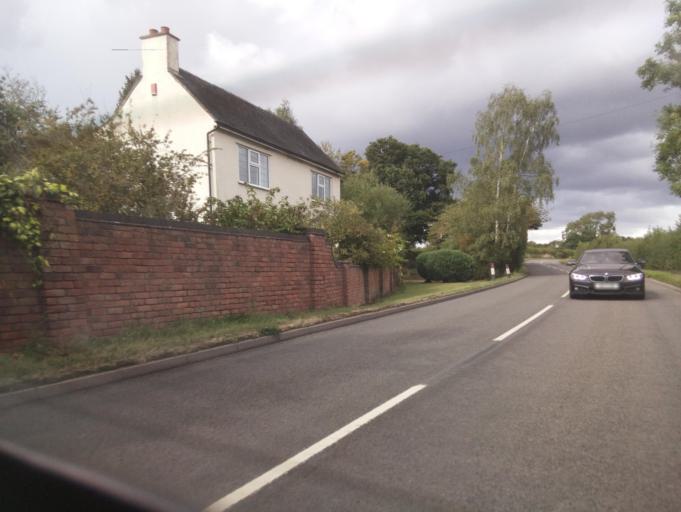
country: GB
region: England
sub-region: Staffordshire
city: Eccleshall
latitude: 52.8694
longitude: -2.2491
